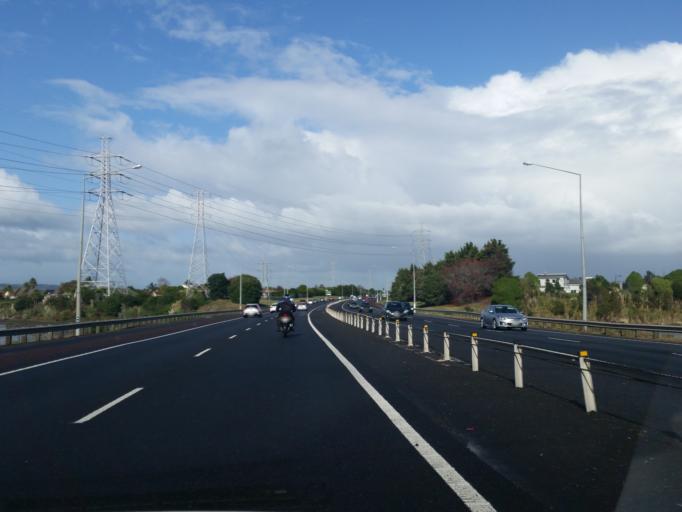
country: NZ
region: Auckland
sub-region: Auckland
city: Papakura
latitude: -37.0592
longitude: 174.9229
